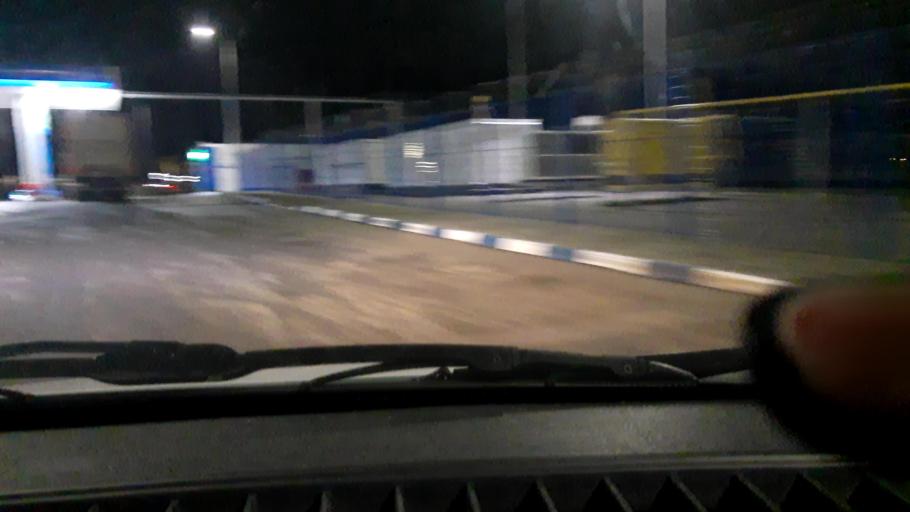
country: RU
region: Bashkortostan
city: Ufa
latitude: 54.5922
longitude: 55.9102
